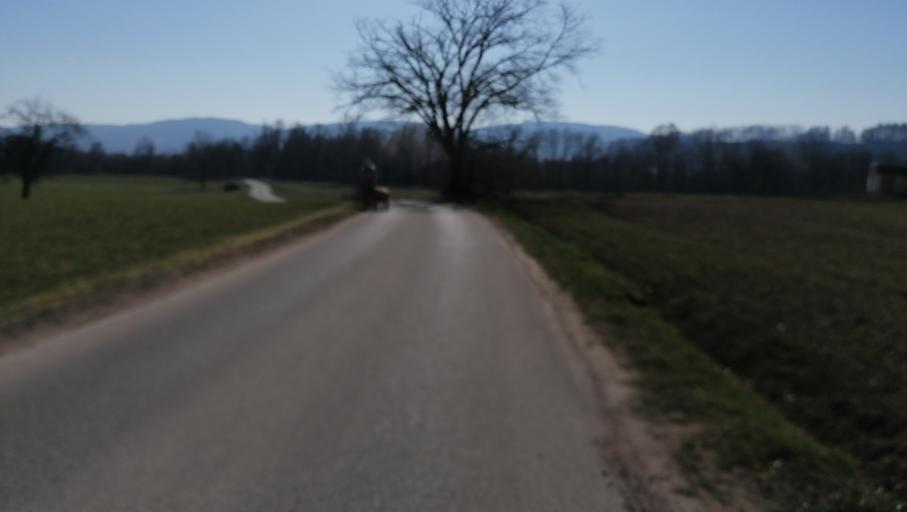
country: CH
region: Aargau
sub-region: Bezirk Rheinfelden
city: Mumpf
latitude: 47.5768
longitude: 7.9175
